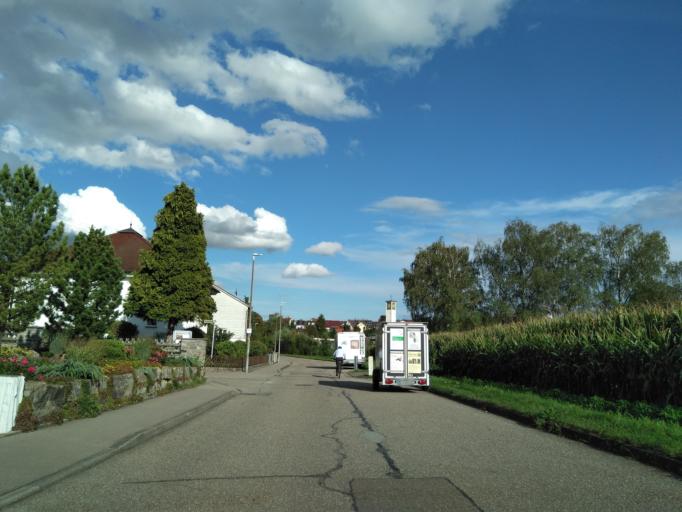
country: DE
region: Baden-Wuerttemberg
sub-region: Regierungsbezirk Stuttgart
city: Sersheim
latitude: 48.9579
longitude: 9.0096
